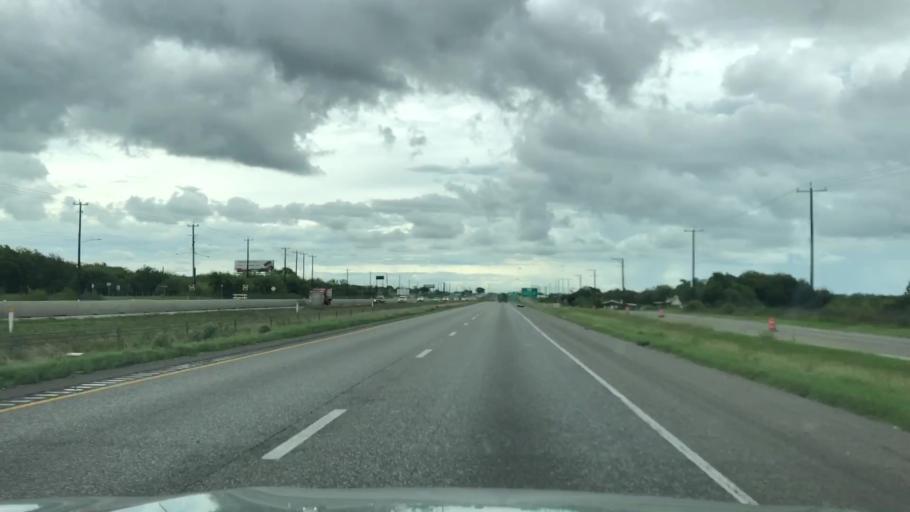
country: US
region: Texas
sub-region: Bexar County
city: Converse
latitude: 29.4615
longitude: -98.3062
